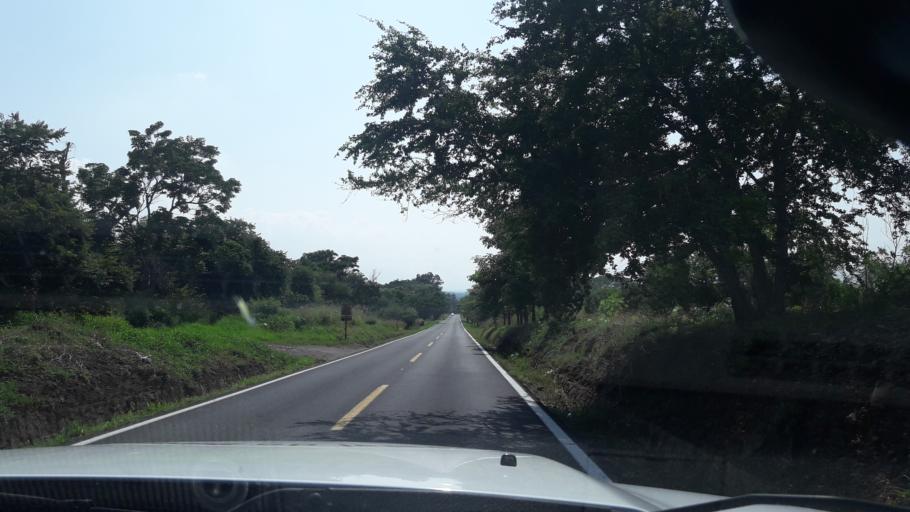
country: MX
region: Colima
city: Comala
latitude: 19.3367
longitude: -103.7461
